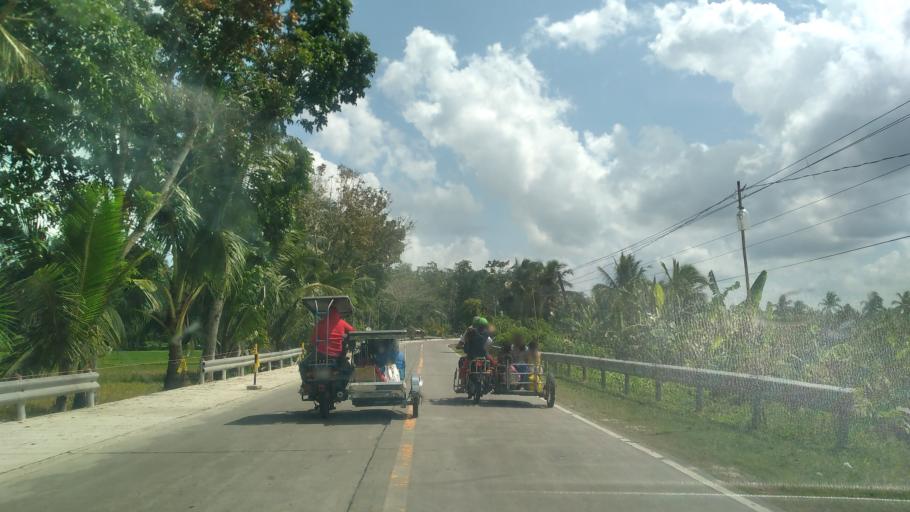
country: PH
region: Calabarzon
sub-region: Province of Quezon
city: Macalelon
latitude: 13.7569
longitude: 122.1476
